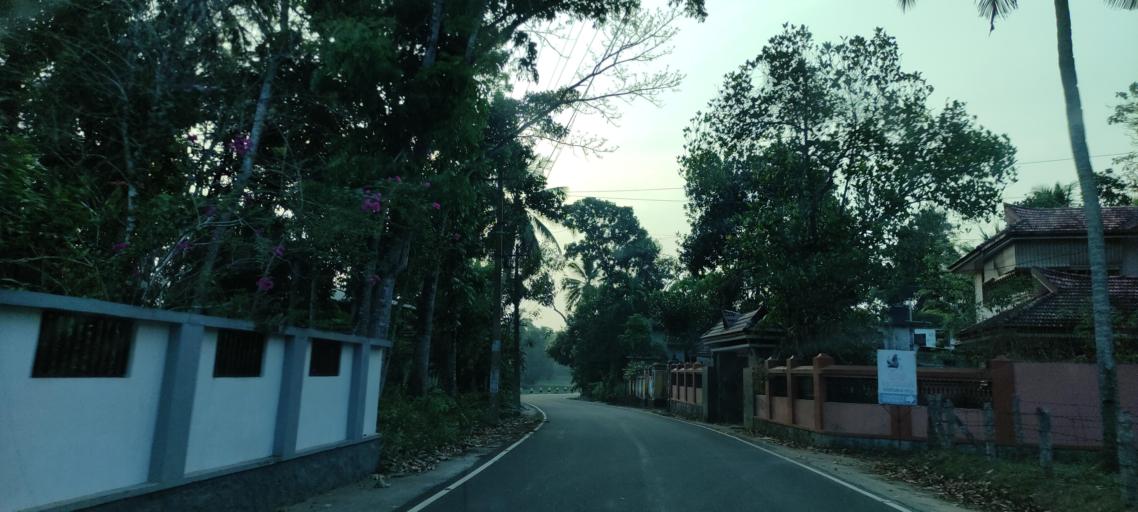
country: IN
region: Kerala
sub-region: Alappuzha
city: Mavelikara
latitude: 9.2775
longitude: 76.5581
